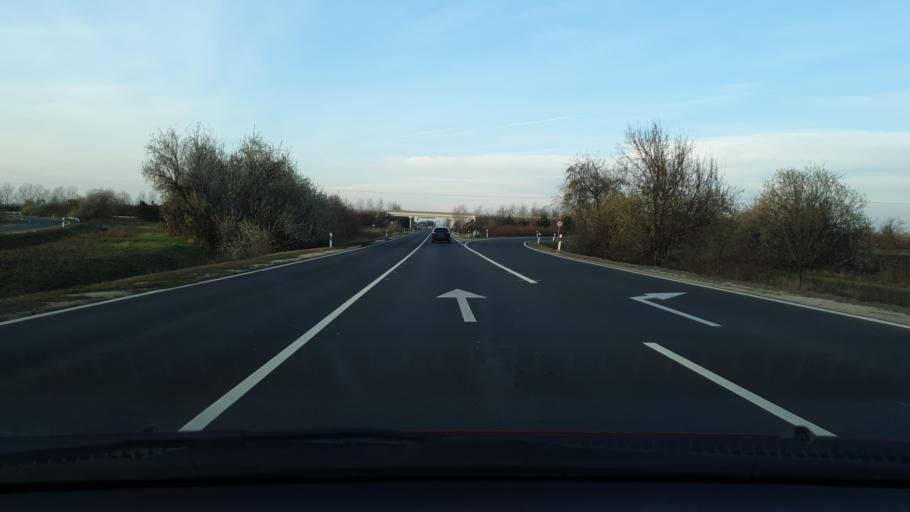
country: HU
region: Jasz-Nagykun-Szolnok
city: Zagyvarekas
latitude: 47.1798
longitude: 20.0998
